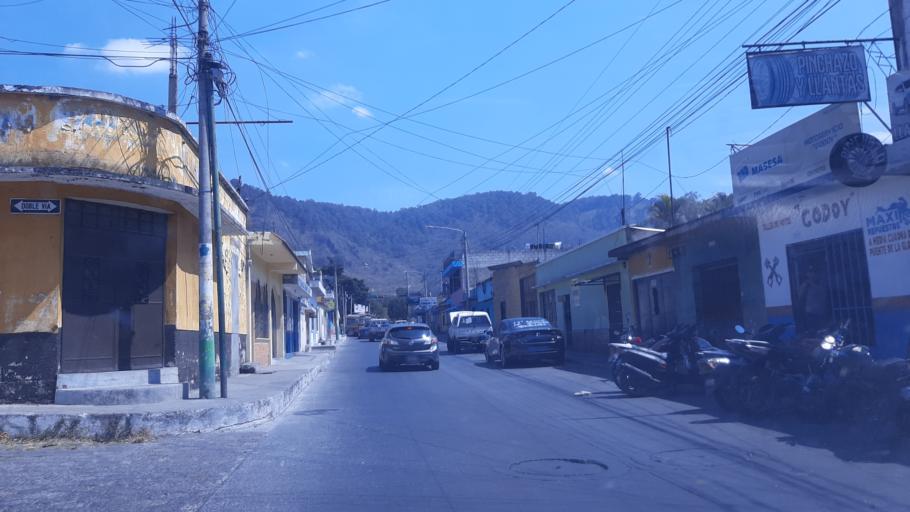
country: GT
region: Guatemala
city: Amatitlan
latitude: 14.4846
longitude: -90.6186
